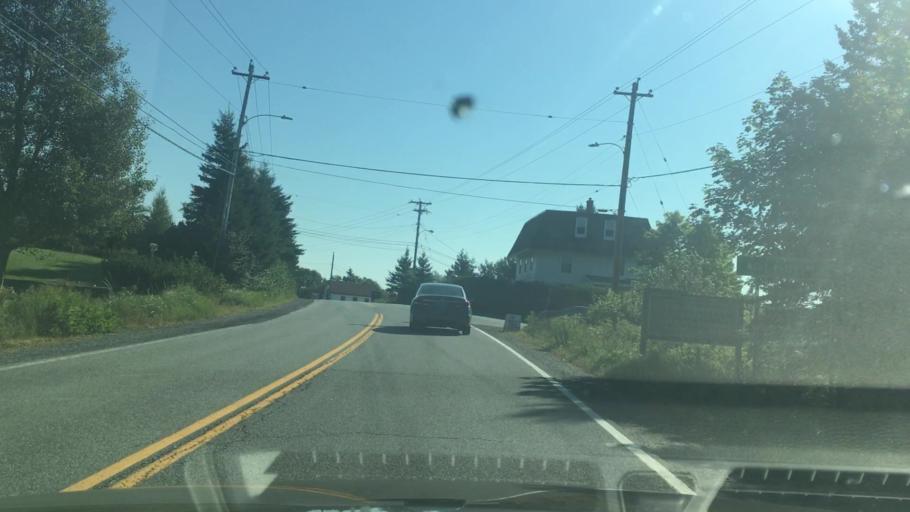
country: CA
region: Nova Scotia
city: Cole Harbour
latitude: 44.7831
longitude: -63.1554
